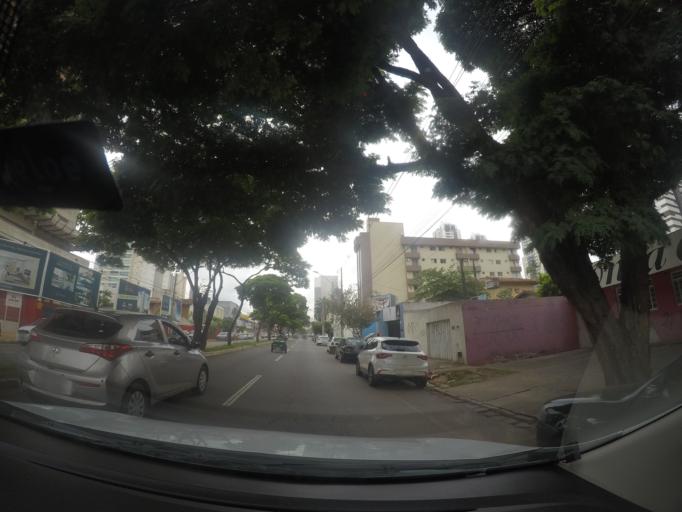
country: BR
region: Goias
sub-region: Goiania
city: Goiania
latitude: -16.7000
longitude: -49.2750
